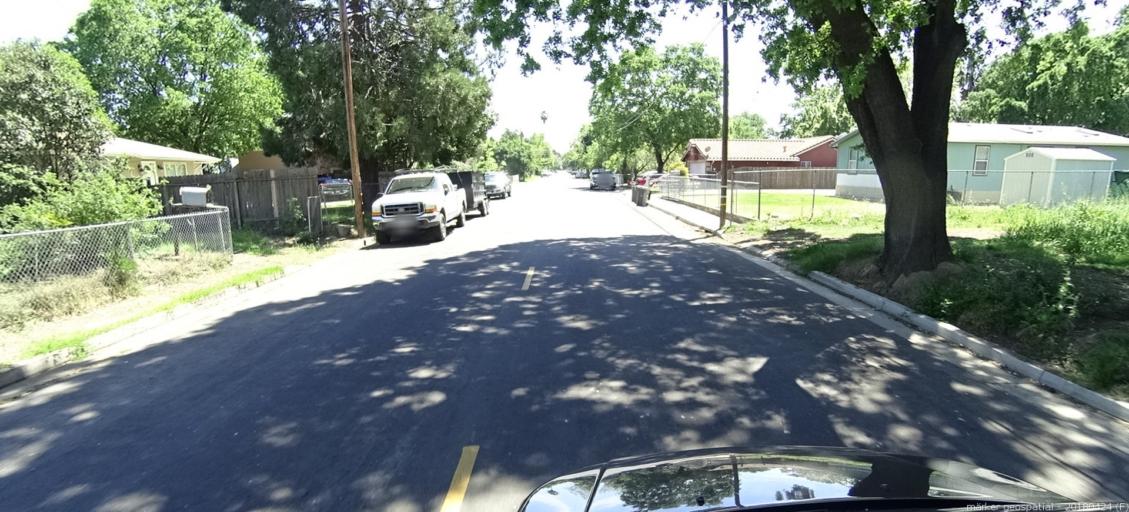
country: US
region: California
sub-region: Yolo County
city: West Sacramento
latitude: 38.5849
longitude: -121.5402
